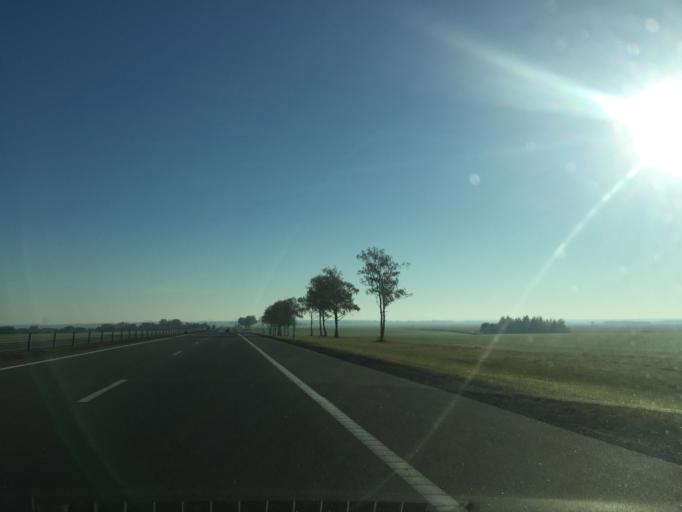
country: BY
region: Minsk
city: Zamostochcha
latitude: 53.7615
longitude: 27.9192
